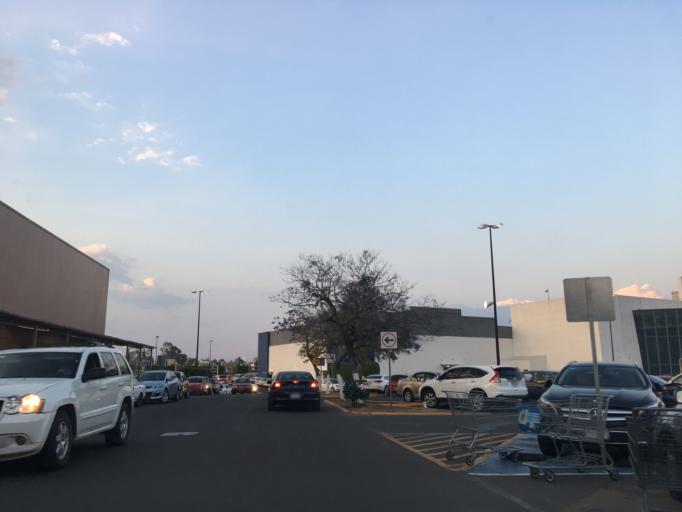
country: MX
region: Michoacan
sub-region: Morelia
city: Morelos
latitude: 19.6797
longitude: -101.2196
